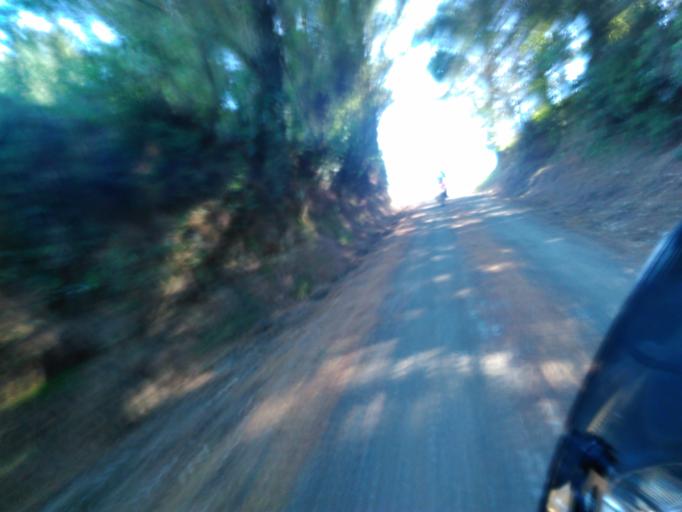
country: NZ
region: Bay of Plenty
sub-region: Opotiki District
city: Opotiki
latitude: -38.3657
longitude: 177.5982
